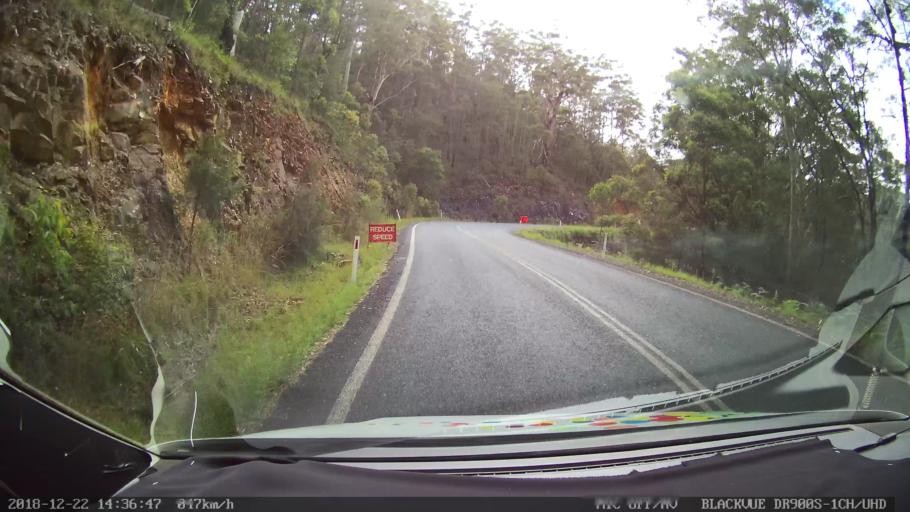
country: AU
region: New South Wales
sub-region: Bellingen
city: Dorrigo
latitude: -30.1304
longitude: 152.6039
